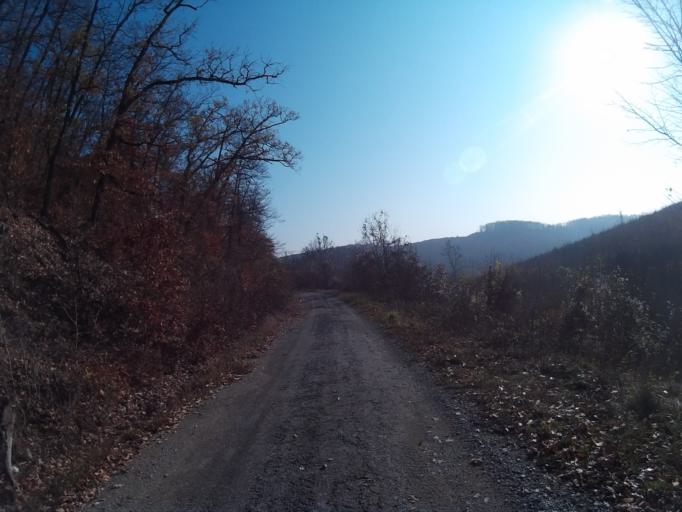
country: HU
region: Heves
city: Felsotarkany
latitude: 47.9964
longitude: 20.3867
